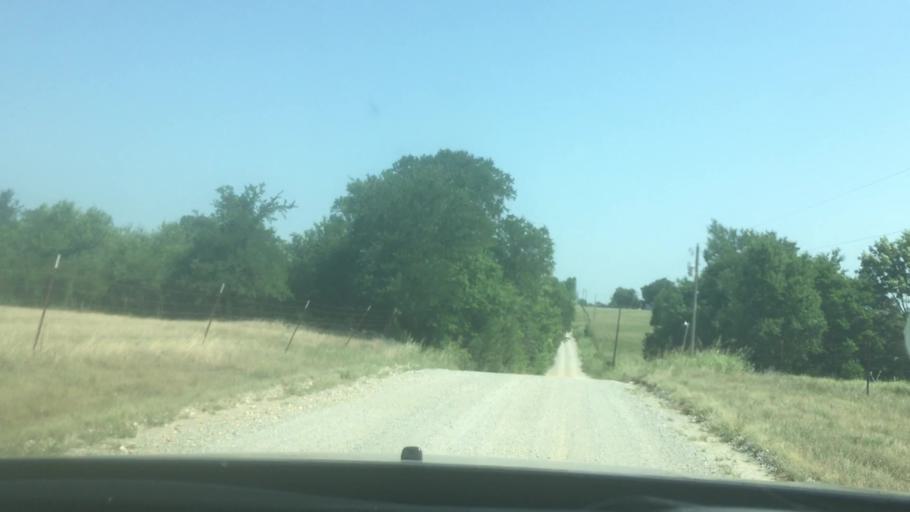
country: US
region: Oklahoma
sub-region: Bryan County
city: Durant
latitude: 34.1349
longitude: -96.4077
